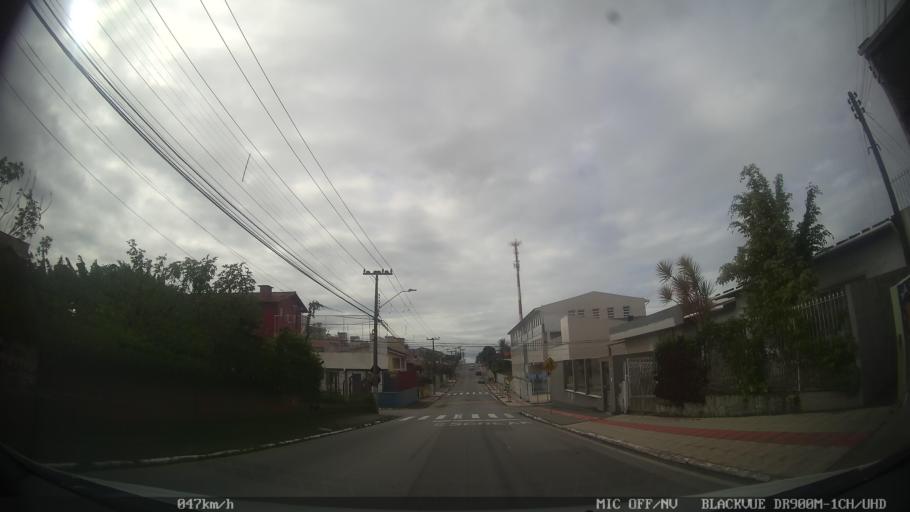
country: BR
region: Santa Catarina
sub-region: Sao Jose
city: Campinas
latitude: -27.5661
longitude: -48.6271
